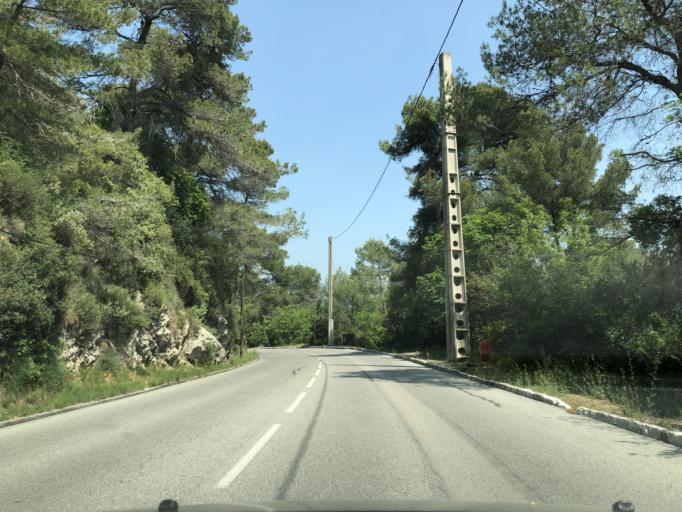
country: FR
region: Provence-Alpes-Cote d'Azur
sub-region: Departement des Alpes-Maritimes
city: La Trinite
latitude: 43.7245
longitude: 7.3033
